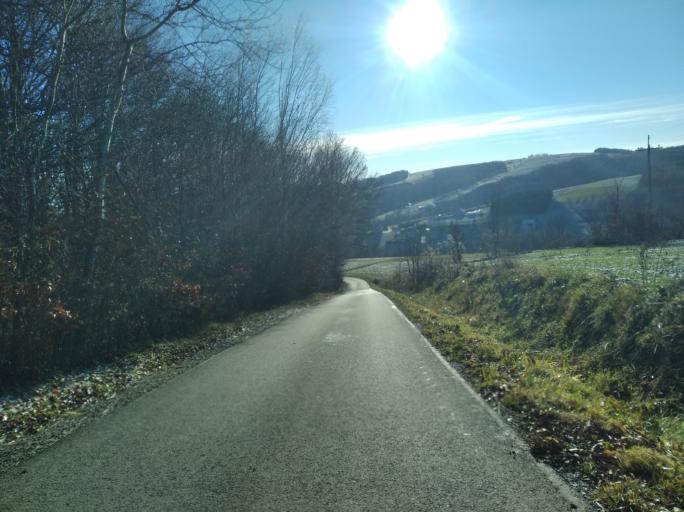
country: PL
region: Subcarpathian Voivodeship
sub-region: Powiat strzyzowski
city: Strzyzow
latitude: 49.9352
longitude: 21.7685
